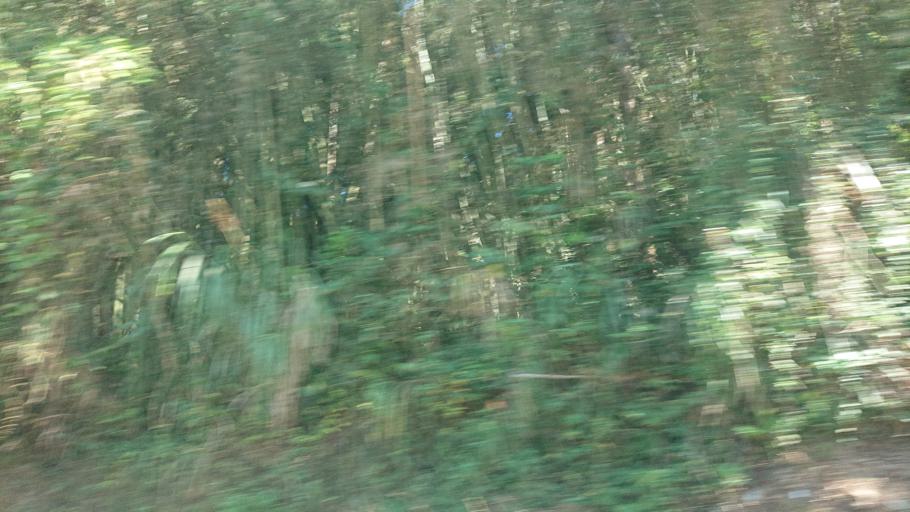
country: TW
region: Taiwan
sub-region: Chiayi
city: Jiayi Shi
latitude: 23.4775
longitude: 120.7180
